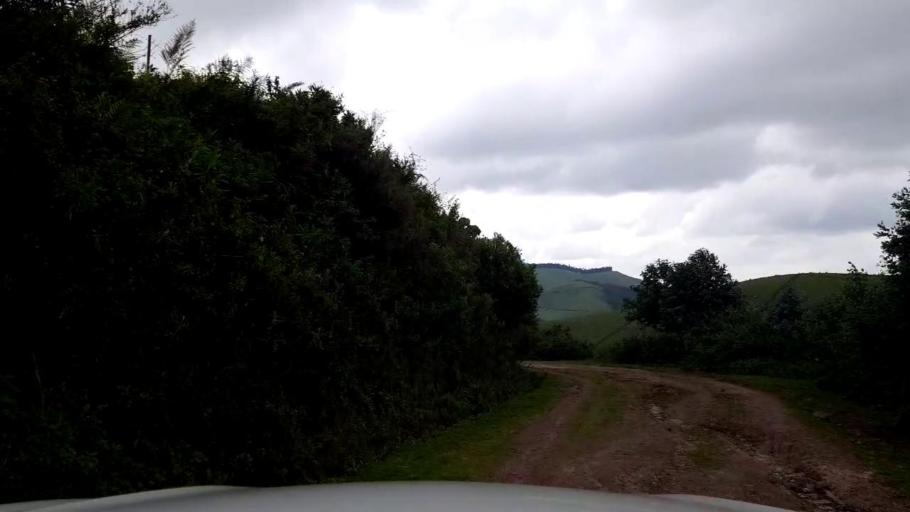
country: RW
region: Western Province
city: Gisenyi
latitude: -1.6769
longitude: 29.4175
